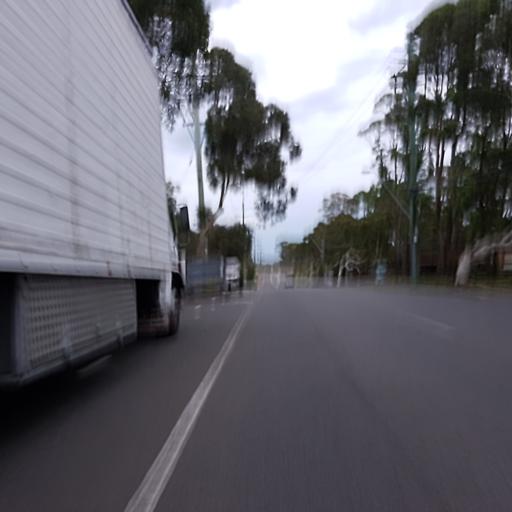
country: AU
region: New South Wales
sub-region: Warringah
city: Allambie Heights
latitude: -33.7559
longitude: 151.2425
